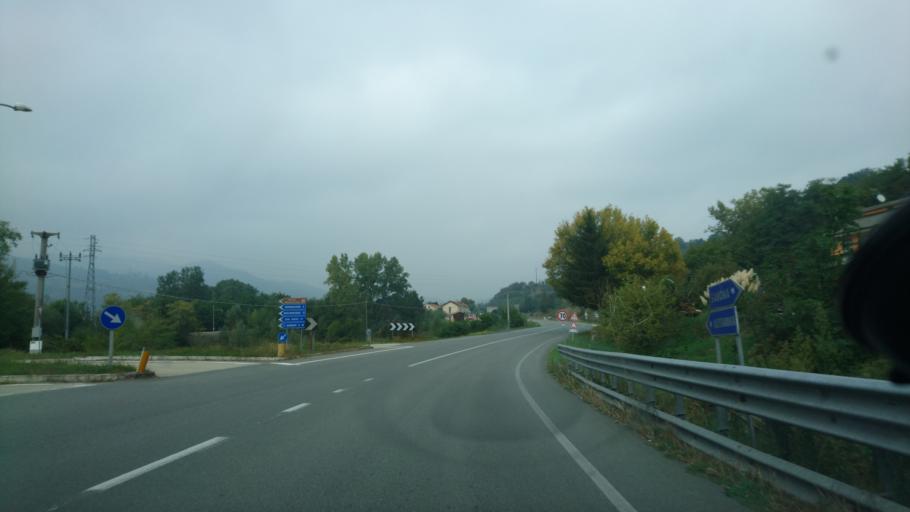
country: IT
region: Piedmont
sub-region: Provincia di Asti
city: Mombaldone
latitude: 44.5784
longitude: 8.3489
